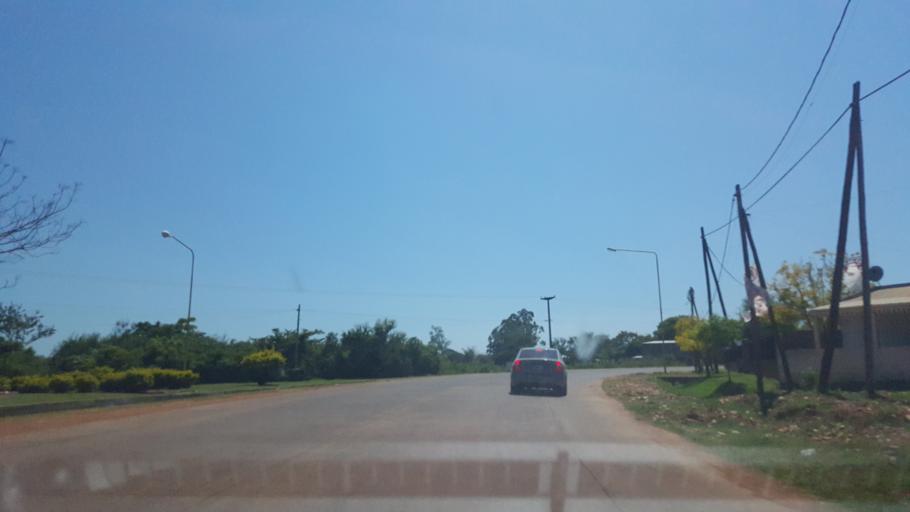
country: AR
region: Corrientes
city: Santo Tome
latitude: -28.5470
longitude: -56.0619
